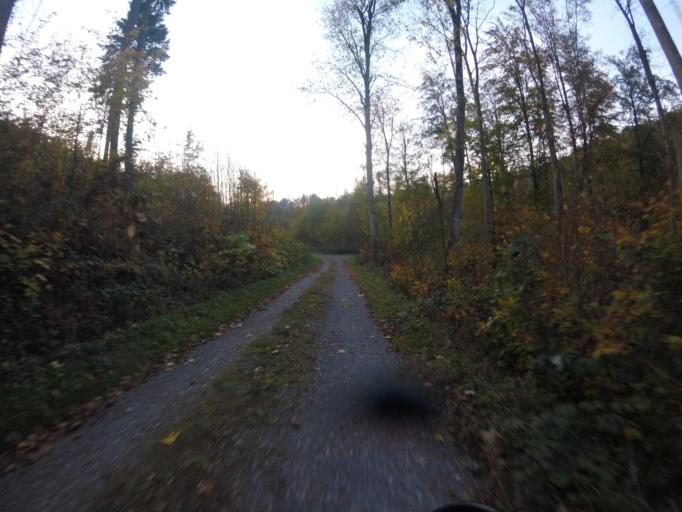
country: DE
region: Baden-Wuerttemberg
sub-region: Regierungsbezirk Stuttgart
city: Oberstenfeld
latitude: 48.9963
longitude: 9.3408
